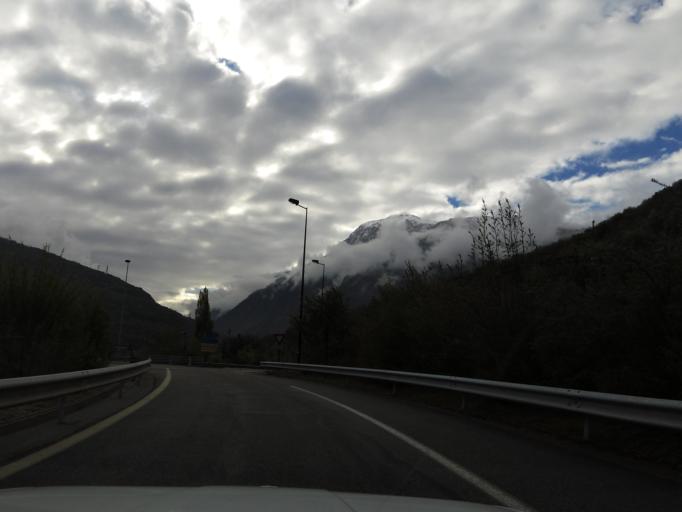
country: FR
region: Rhone-Alpes
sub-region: Departement de la Savoie
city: Saint-Michel-de-Maurienne
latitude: 45.2177
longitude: 6.4607
